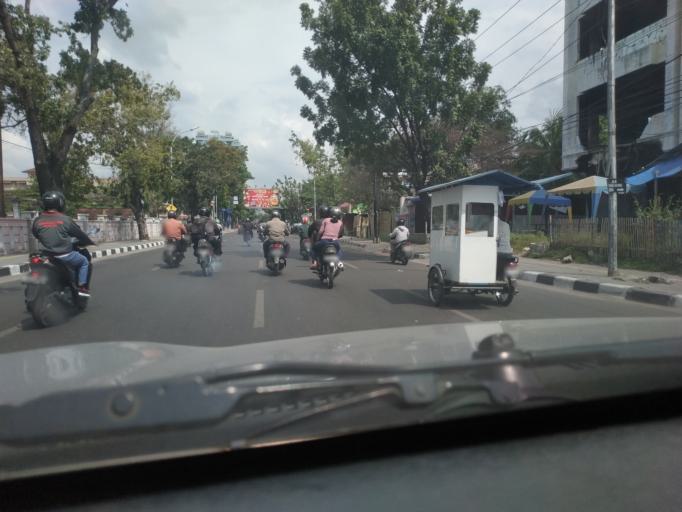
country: ID
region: North Sumatra
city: Medan
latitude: 3.5846
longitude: 98.6619
